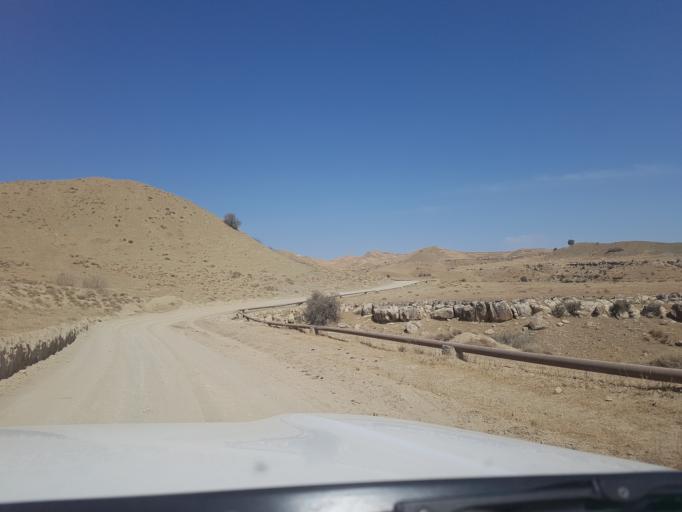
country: TM
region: Ahal
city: Baharly
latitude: 38.2469
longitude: 56.8920
